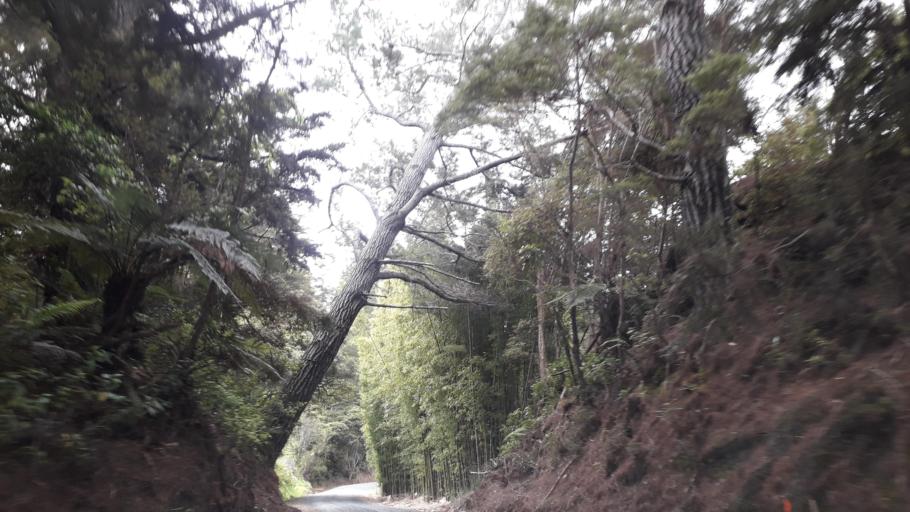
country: NZ
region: Northland
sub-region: Far North District
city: Taipa
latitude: -35.0809
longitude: 173.5519
